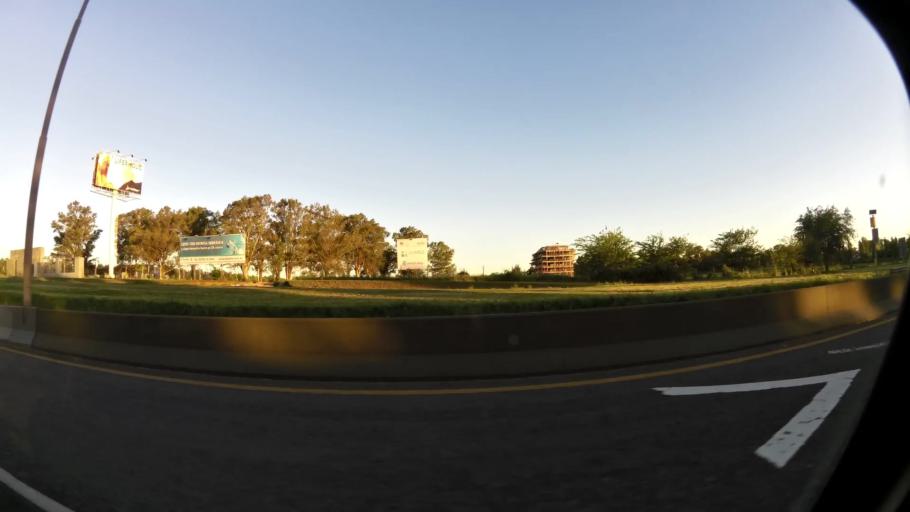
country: AR
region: Buenos Aires
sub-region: Partido de Quilmes
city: Quilmes
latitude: -34.8085
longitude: -58.1734
